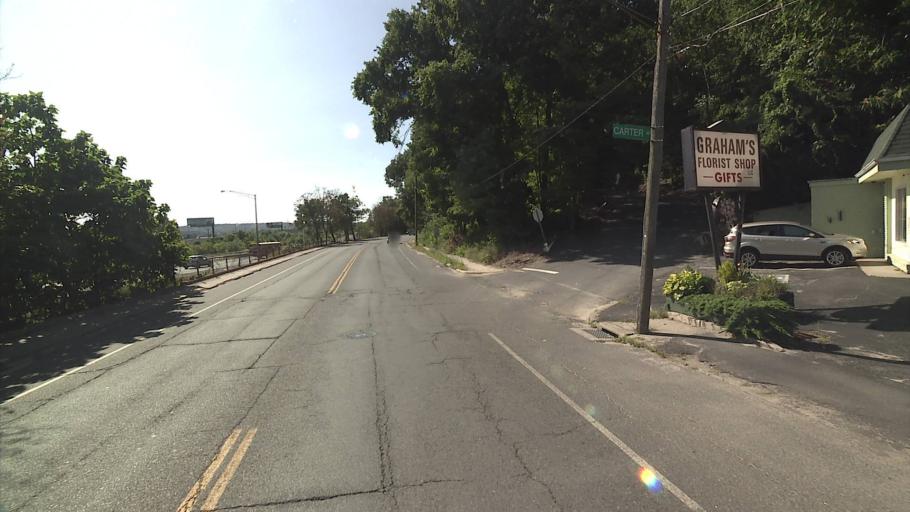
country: US
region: Connecticut
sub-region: New Haven County
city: Waterbury
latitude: 41.5634
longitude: -73.0587
